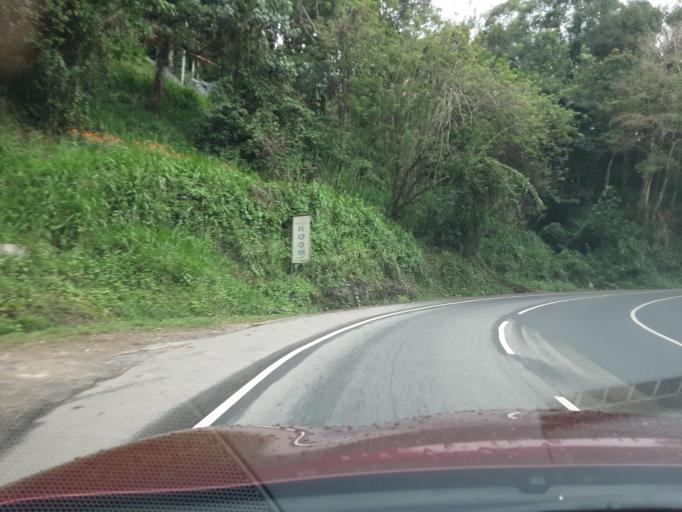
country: LK
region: Uva
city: Badulla
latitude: 7.0187
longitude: 81.0548
